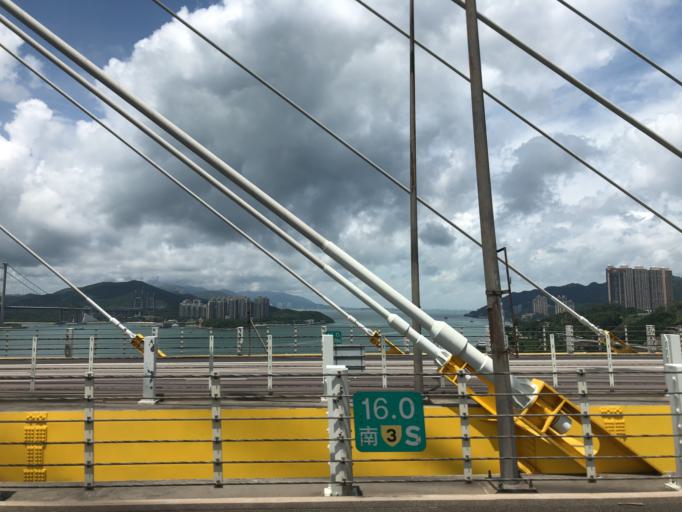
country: HK
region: Tsuen Wan
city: Tsuen Wan
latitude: 22.3655
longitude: 114.0791
